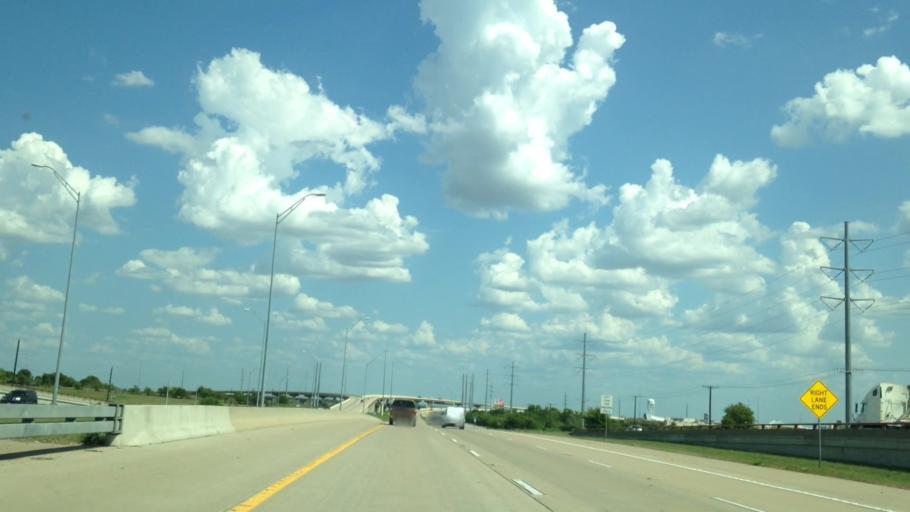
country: US
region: Texas
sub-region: Travis County
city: Pflugerville
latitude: 30.4787
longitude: -97.6031
